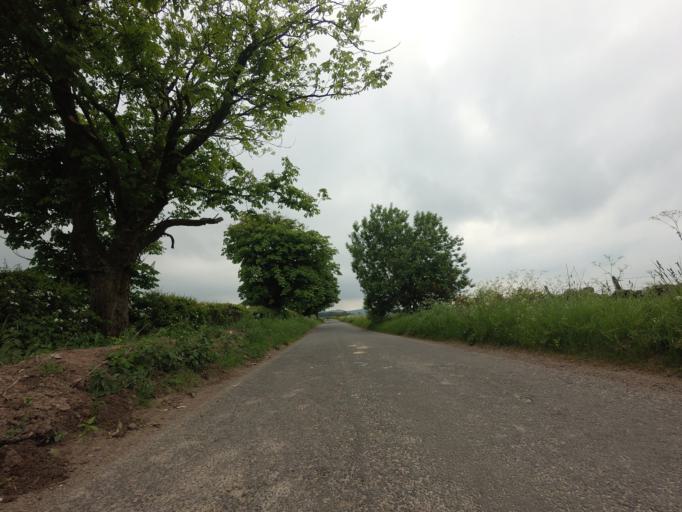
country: GB
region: Scotland
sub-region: Perth and Kinross
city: Kinross
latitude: 56.1914
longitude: -3.4345
